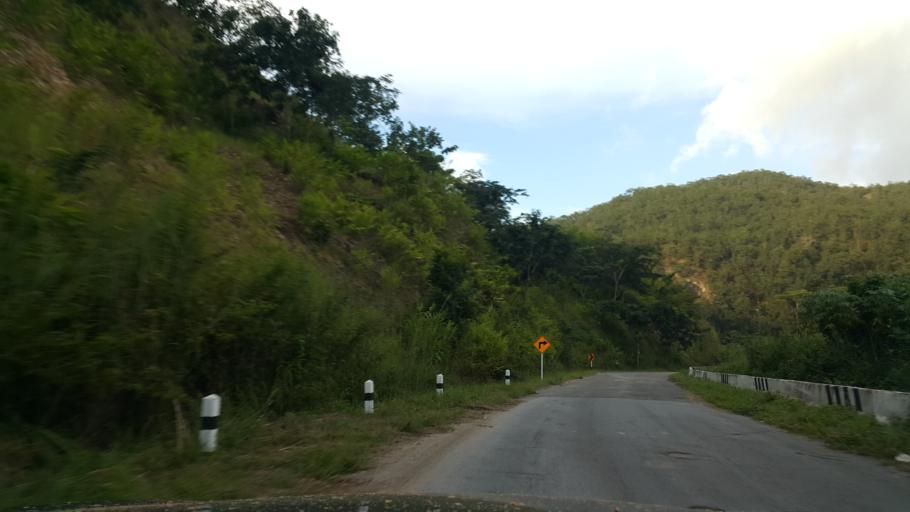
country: TH
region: Mae Hong Son
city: Mae Hi
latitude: 19.2021
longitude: 98.4302
